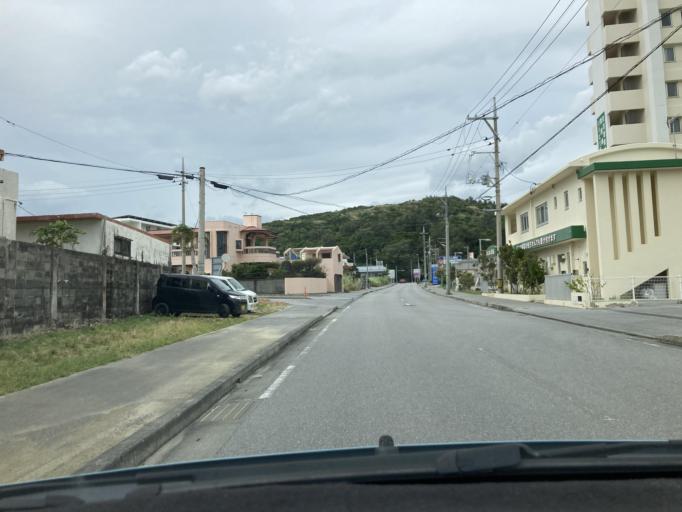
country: JP
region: Okinawa
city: Ginowan
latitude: 26.1864
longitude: 127.7762
